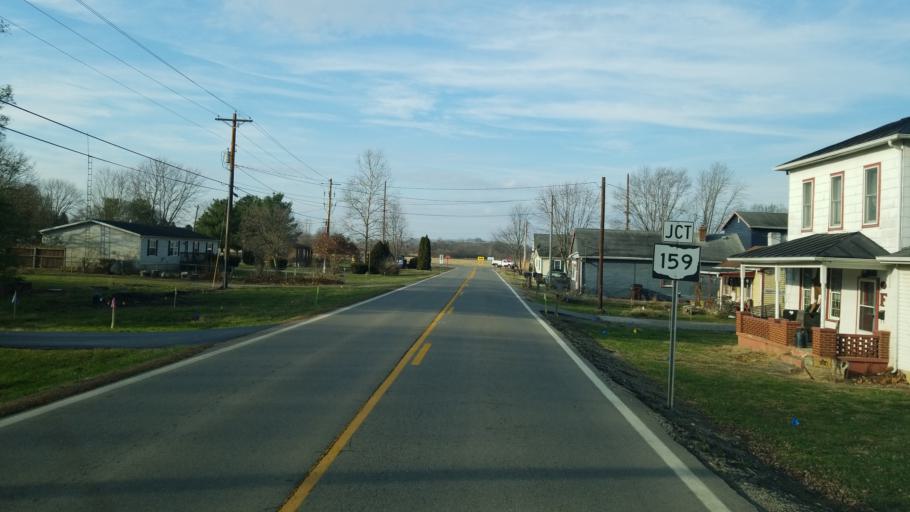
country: US
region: Ohio
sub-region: Ross County
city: Kingston
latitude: 39.4258
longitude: -82.9522
